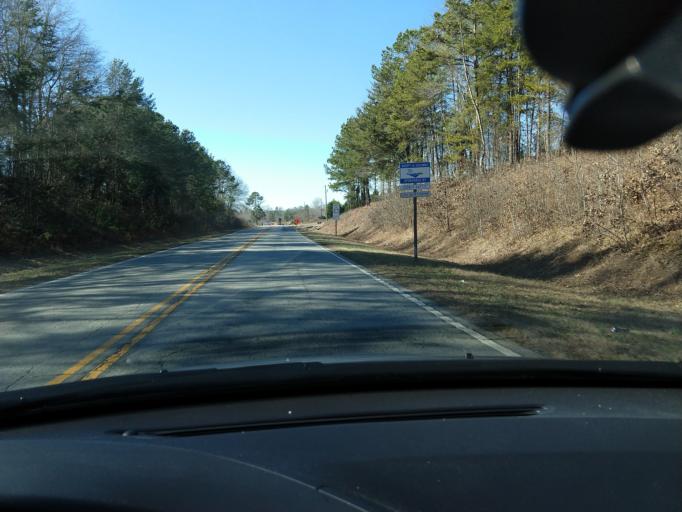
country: US
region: South Carolina
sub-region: Oconee County
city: Westminster
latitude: 34.6690
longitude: -83.1106
